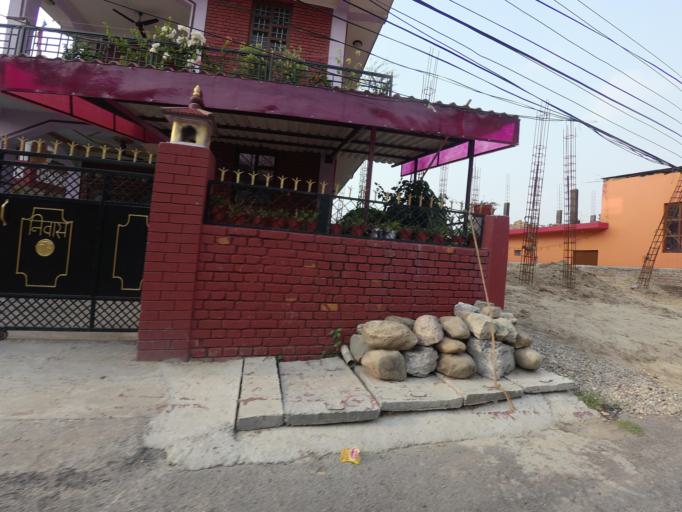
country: NP
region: Western Region
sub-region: Lumbini Zone
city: Bhairahawa
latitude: 27.5068
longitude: 83.4604
